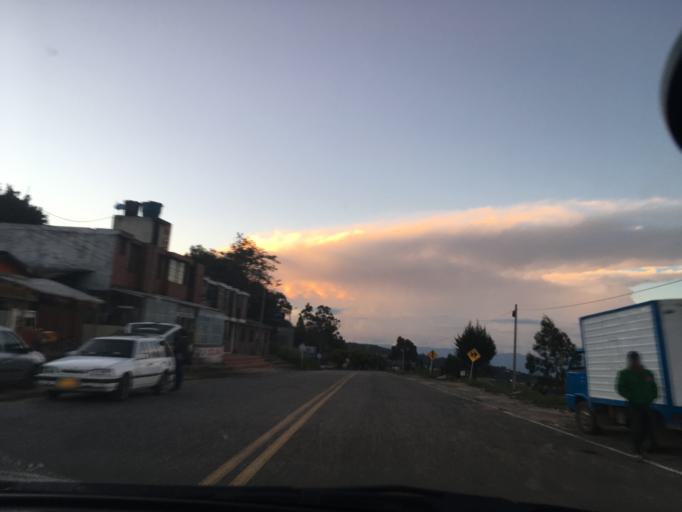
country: CO
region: Boyaca
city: Sogamoso
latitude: 5.6186
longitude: -72.9060
